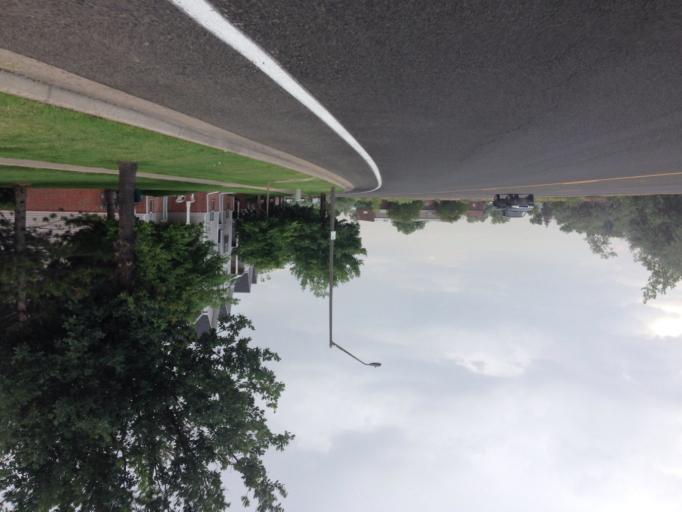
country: US
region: Colorado
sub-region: Larimer County
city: Fort Collins
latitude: 40.5887
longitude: -105.0559
